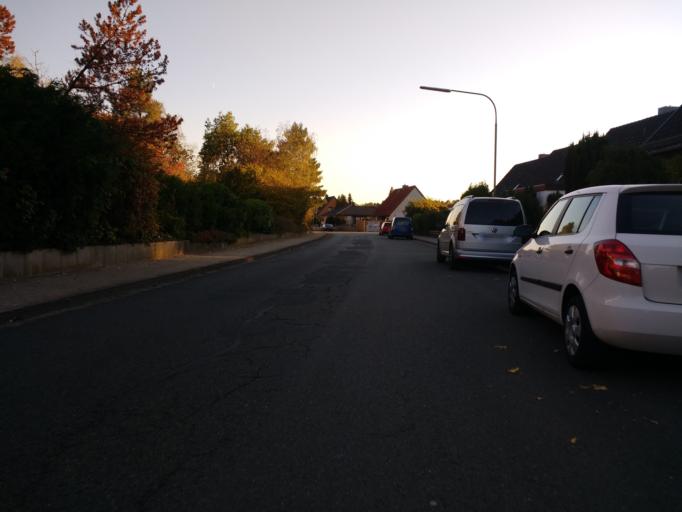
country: DE
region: Lower Saxony
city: Gifhorn
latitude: 52.4839
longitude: 10.5611
